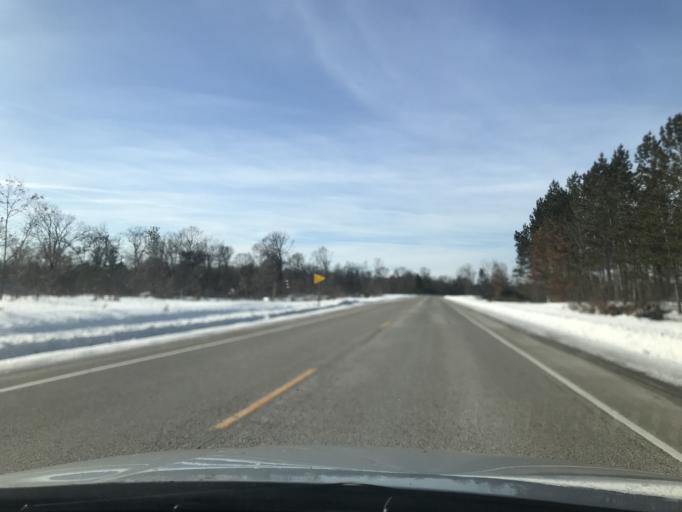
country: US
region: Wisconsin
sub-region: Oconto County
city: Gillett
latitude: 45.1147
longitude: -88.3710
